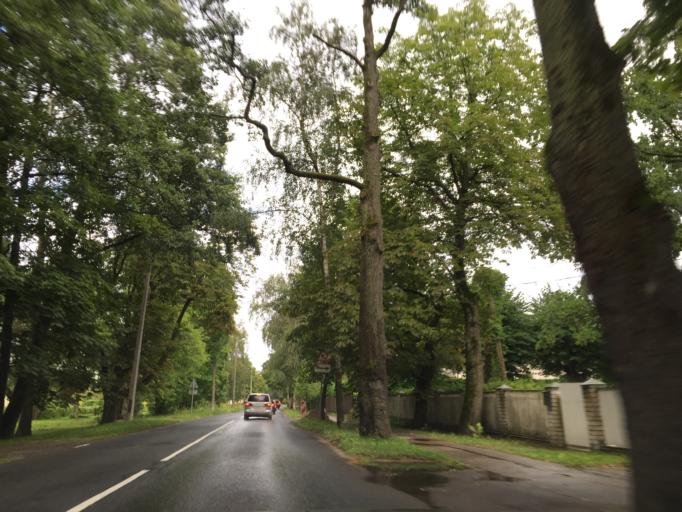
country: LV
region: Marupe
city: Marupe
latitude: 56.9534
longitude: 23.9934
